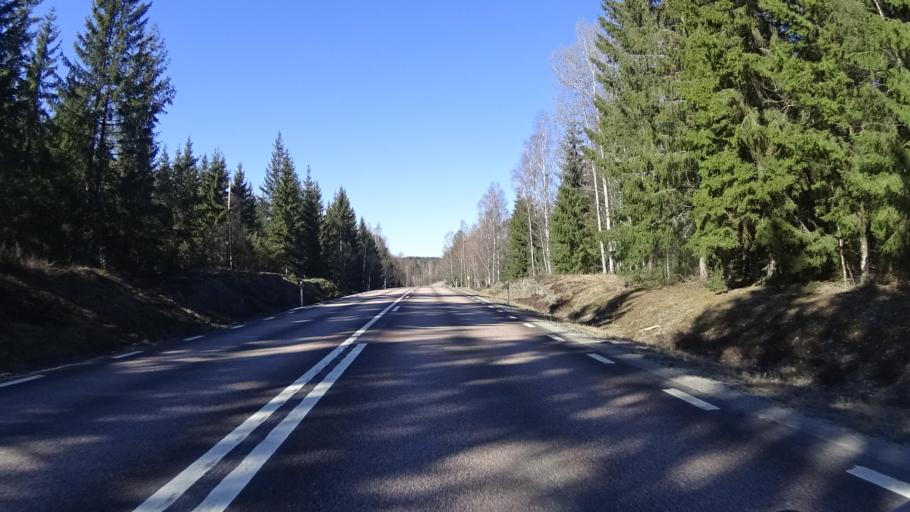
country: SE
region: Vaermland
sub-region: Sunne Kommun
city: Sunne
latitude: 59.6402
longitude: 12.9455
